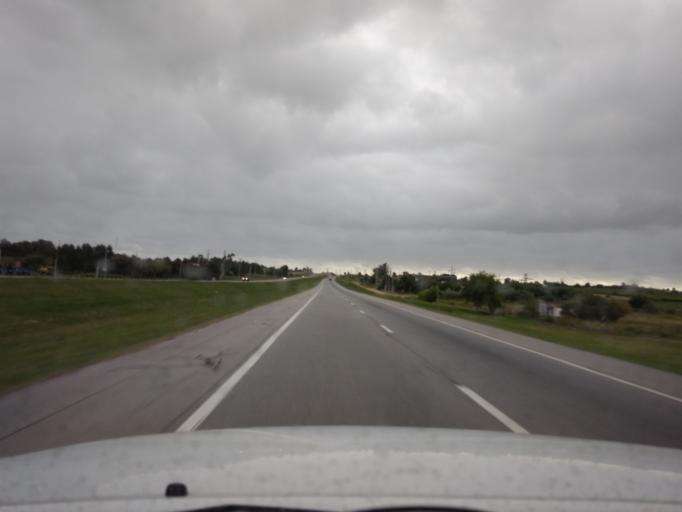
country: UY
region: Canelones
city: Las Piedras
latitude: -34.7087
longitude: -56.2422
